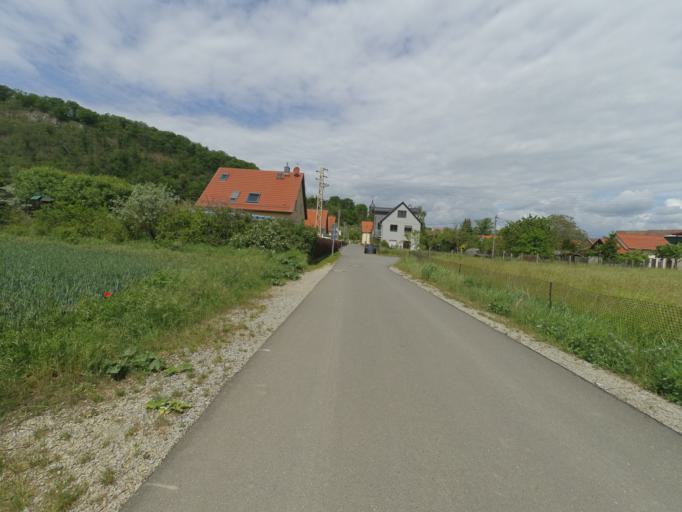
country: DE
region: Thuringia
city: Rothenstein
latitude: 50.8443
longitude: 11.6036
